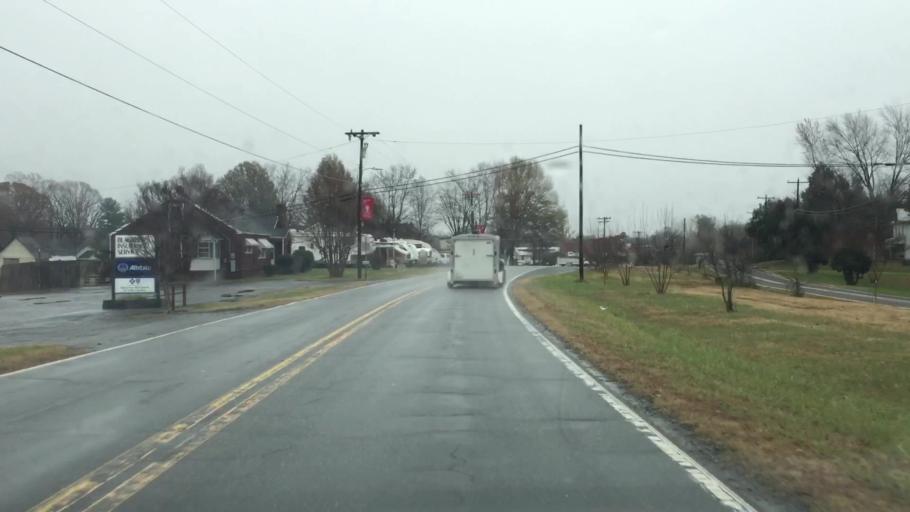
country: US
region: North Carolina
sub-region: Guilford County
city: Stokesdale
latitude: 36.2441
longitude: -79.9876
